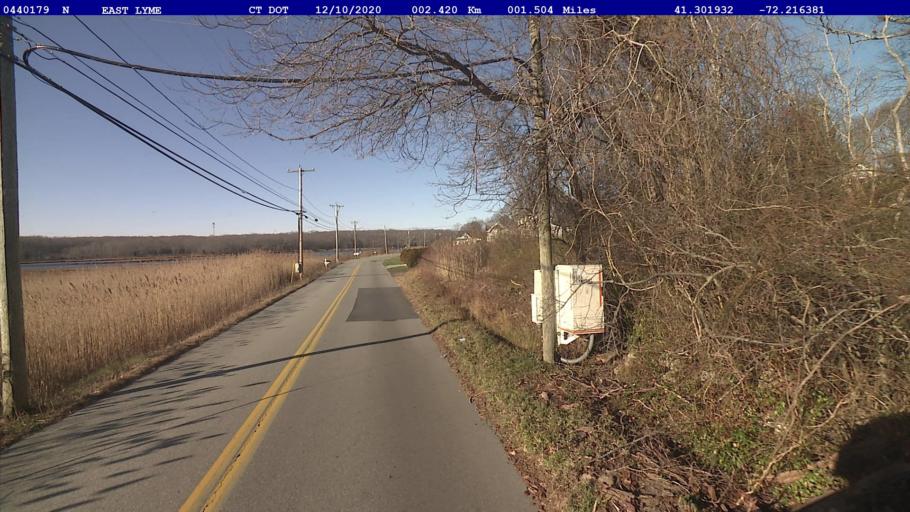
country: US
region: Connecticut
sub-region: New London County
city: Niantic
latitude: 41.3019
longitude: -72.2164
